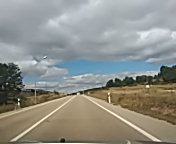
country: ES
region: Castille and Leon
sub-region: Provincia de Soria
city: San Leonardo de Yague
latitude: 41.8338
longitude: -3.0762
